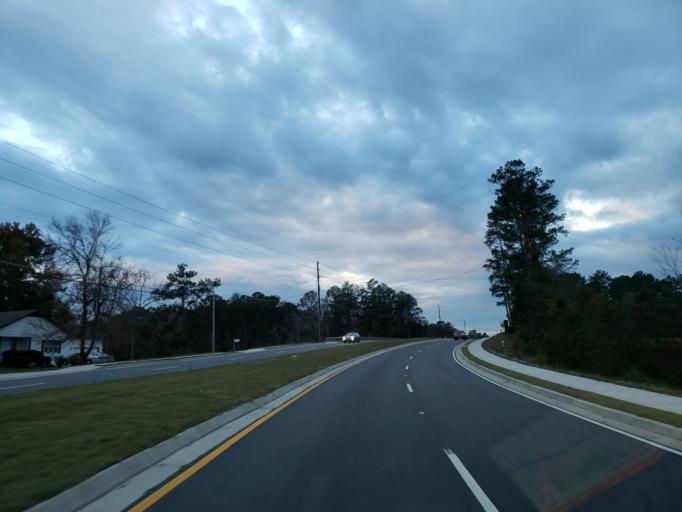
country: US
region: Georgia
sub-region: Cobb County
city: Acworth
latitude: 34.0575
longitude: -84.7346
